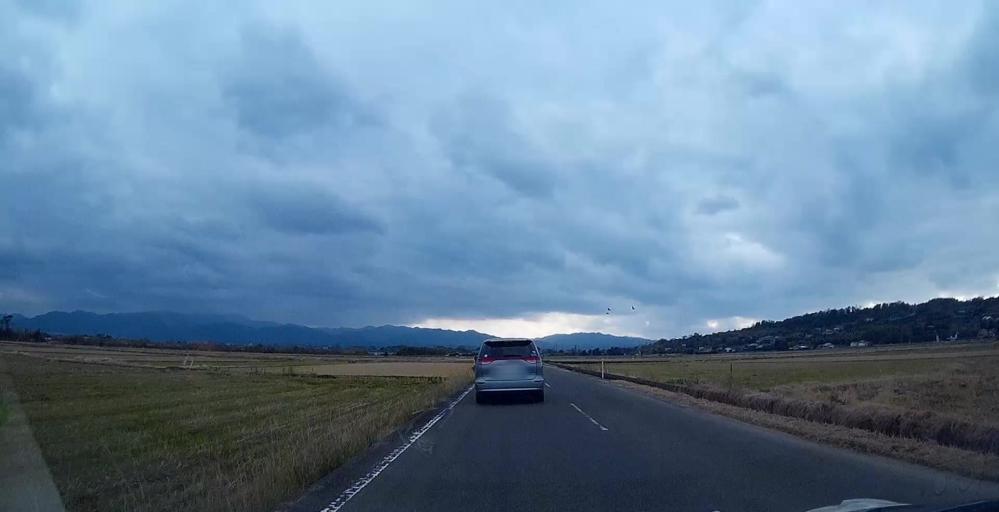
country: JP
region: Kagoshima
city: Izumi
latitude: 32.1009
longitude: 130.2751
